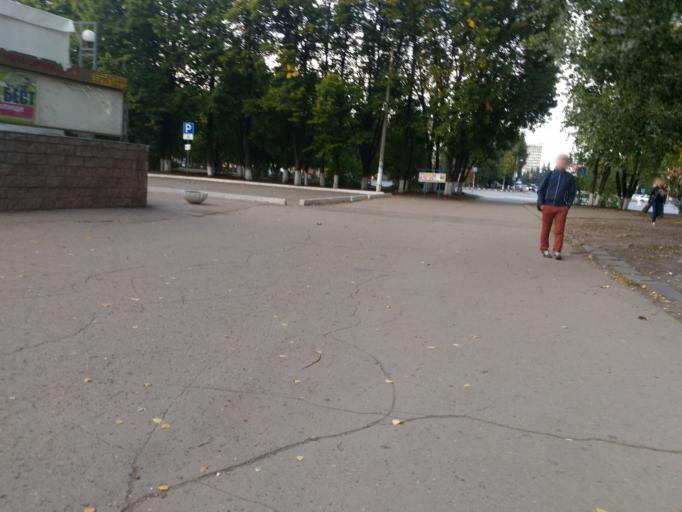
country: RU
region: Ulyanovsk
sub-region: Ulyanovskiy Rayon
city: Ulyanovsk
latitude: 54.3029
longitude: 48.3303
